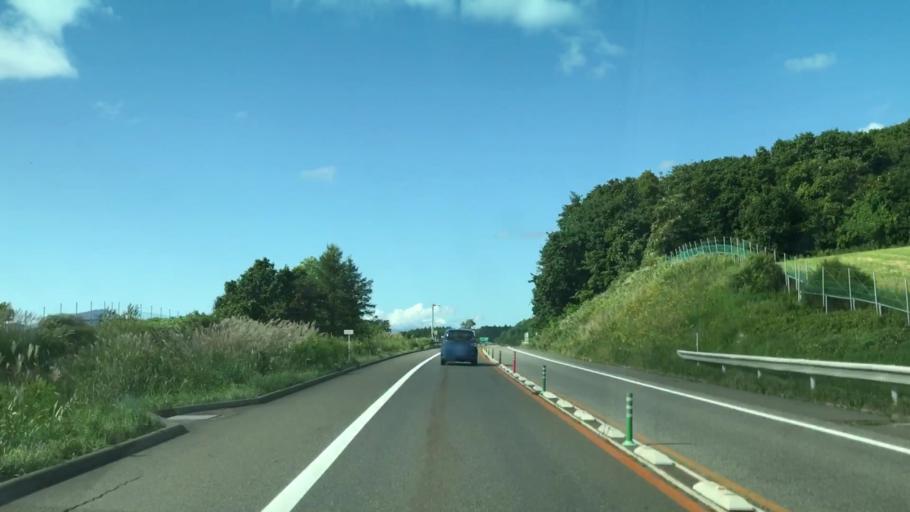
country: JP
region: Hokkaido
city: Date
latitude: 42.4483
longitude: 140.9136
